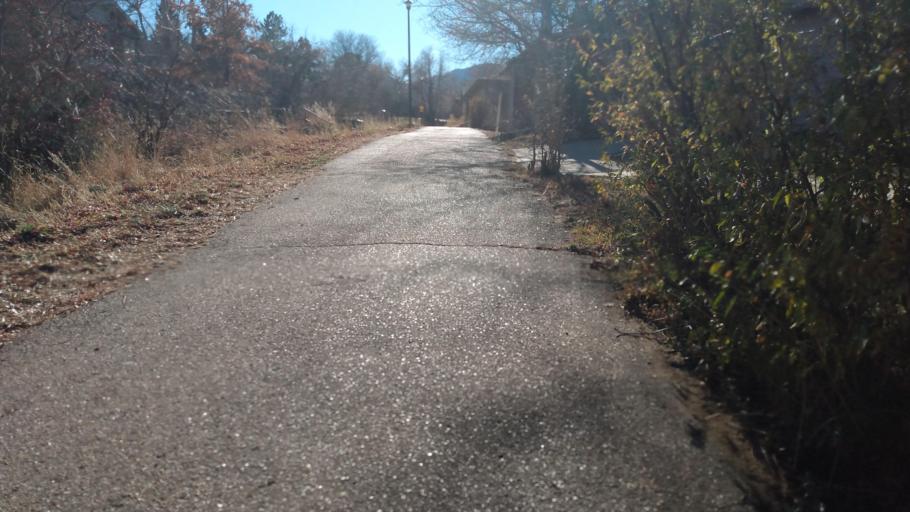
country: US
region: Colorado
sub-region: Boulder County
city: Boulder
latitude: 39.9784
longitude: -105.2464
